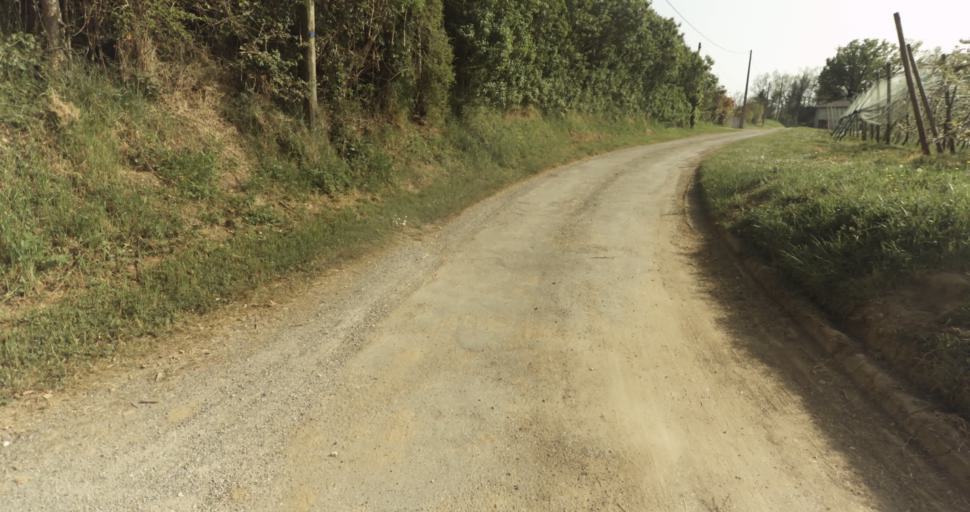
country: FR
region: Midi-Pyrenees
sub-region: Departement du Tarn-et-Garonne
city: Moissac
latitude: 44.1188
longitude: 1.1624
